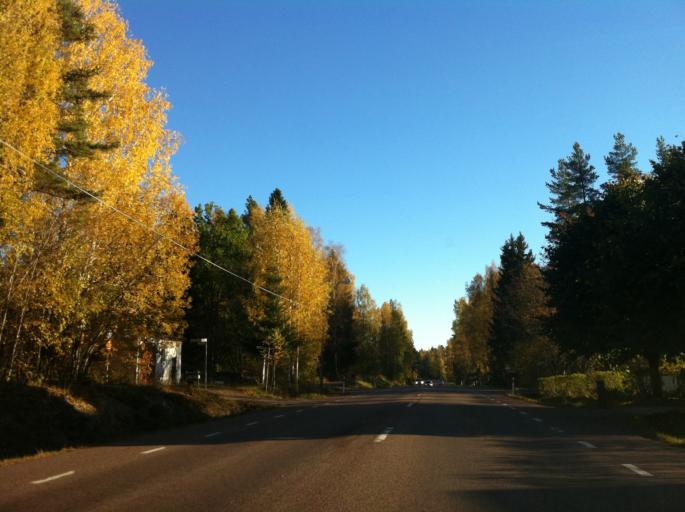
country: SE
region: Dalarna
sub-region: Faluns Kommun
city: Grycksbo
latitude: 60.6952
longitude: 15.4835
